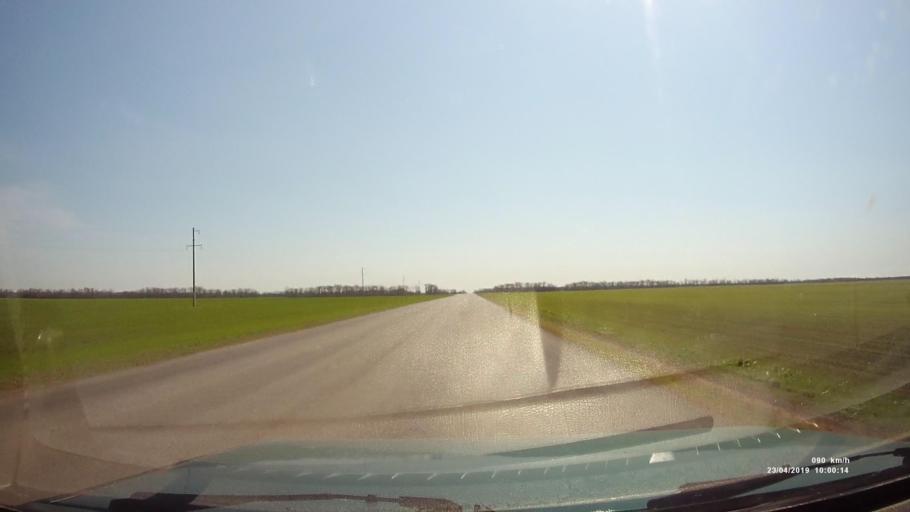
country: RU
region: Rostov
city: Sovetskoye
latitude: 46.7715
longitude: 42.1275
